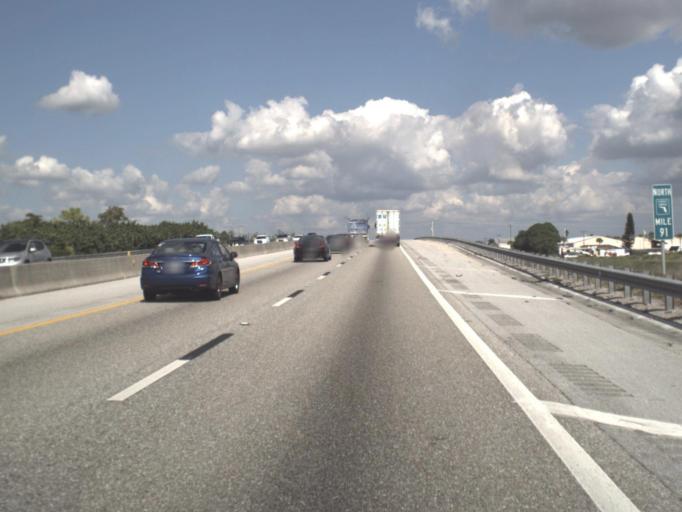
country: US
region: Florida
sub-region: Palm Beach County
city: Greenacres City
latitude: 26.5864
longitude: -80.1732
